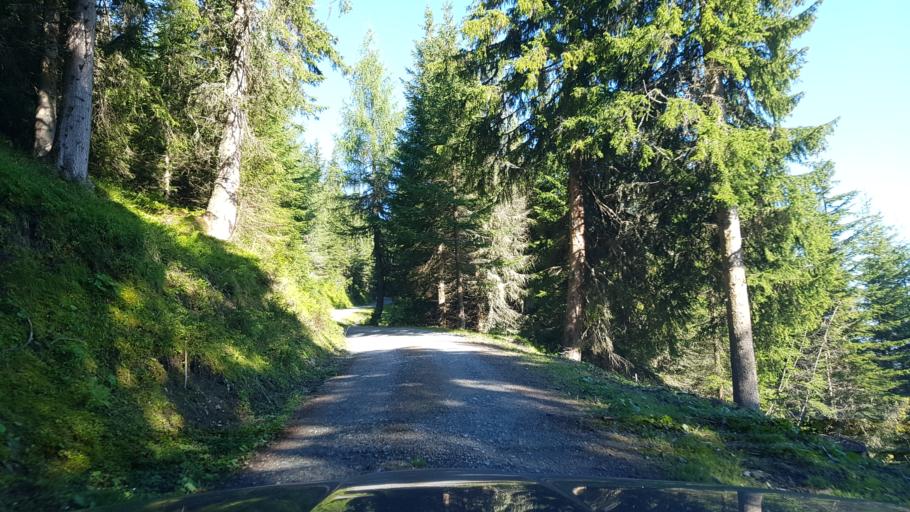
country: AT
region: Salzburg
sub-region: Politischer Bezirk Sankt Johann im Pongau
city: Dorfgastein
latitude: 47.2434
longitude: 13.0719
